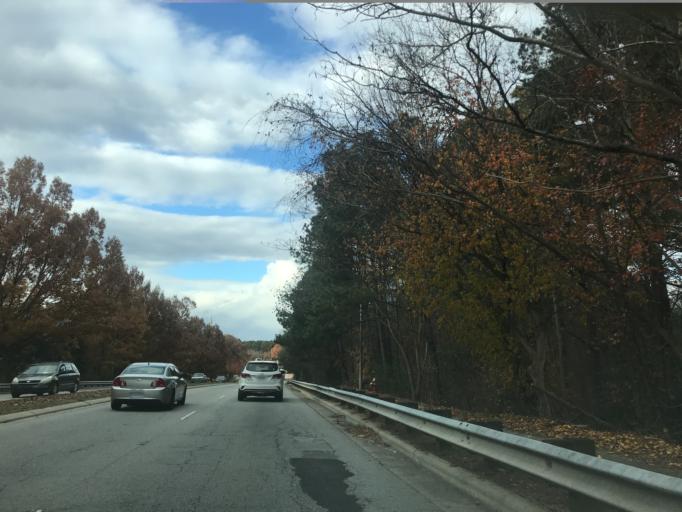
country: US
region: North Carolina
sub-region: Wake County
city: Raleigh
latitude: 35.8393
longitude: -78.5716
